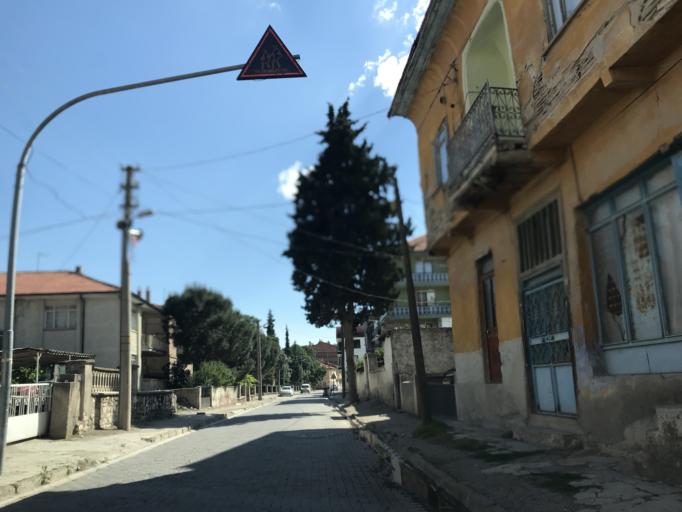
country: TR
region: Denizli
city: Civril
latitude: 38.3017
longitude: 29.7435
